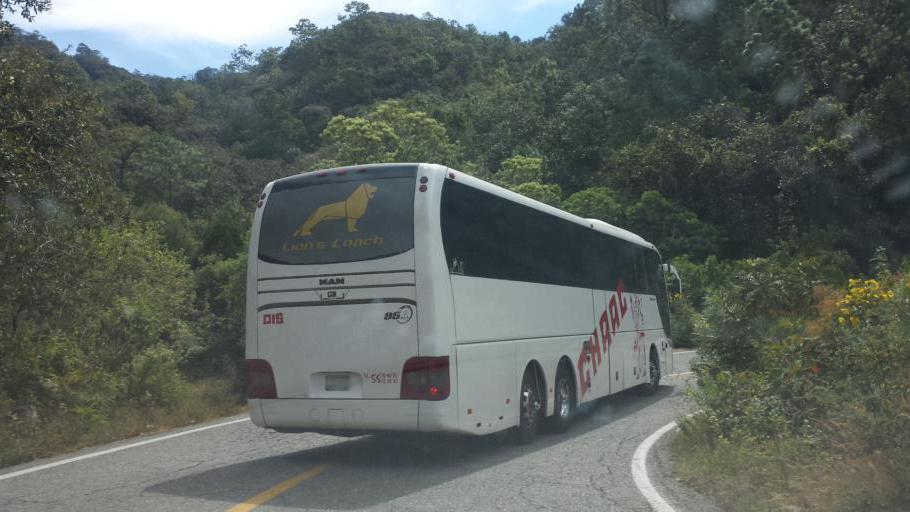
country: MX
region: Oaxaca
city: San Francisco Sola
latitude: 16.4621
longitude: -97.0244
